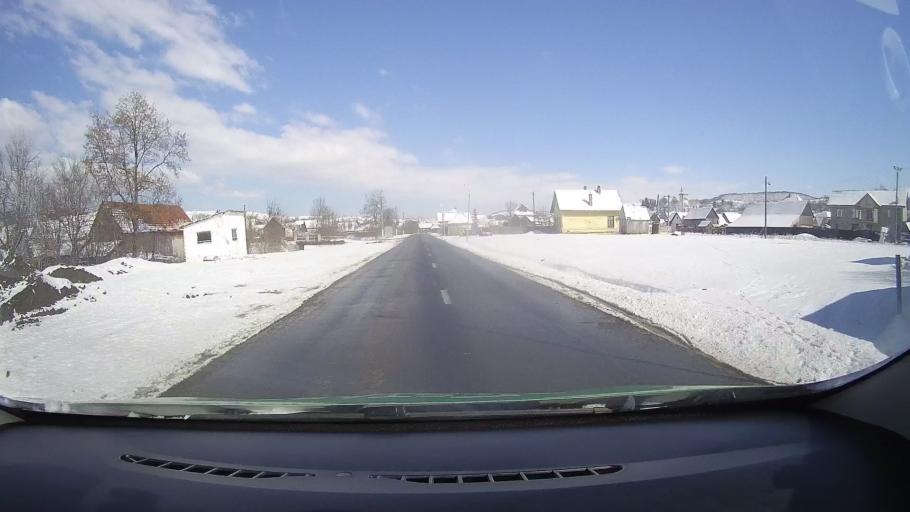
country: RO
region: Sibiu
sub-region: Comuna Vurpar
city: Vurpar
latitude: 45.8916
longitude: 24.3377
